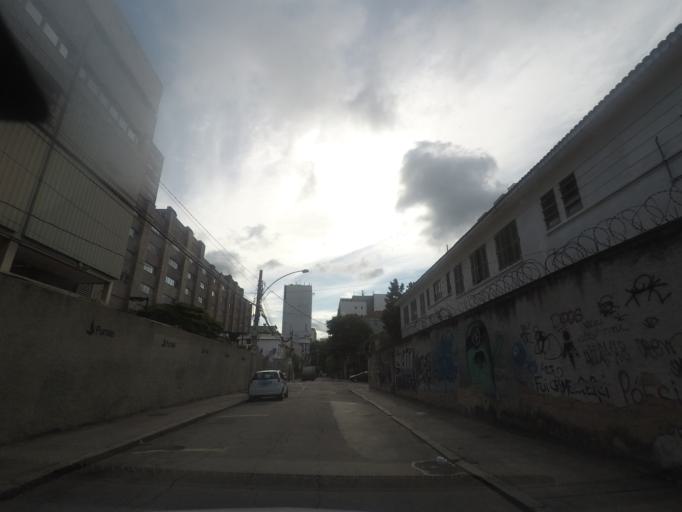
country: BR
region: Rio de Janeiro
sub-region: Rio De Janeiro
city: Rio de Janeiro
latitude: -22.9549
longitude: -43.1909
